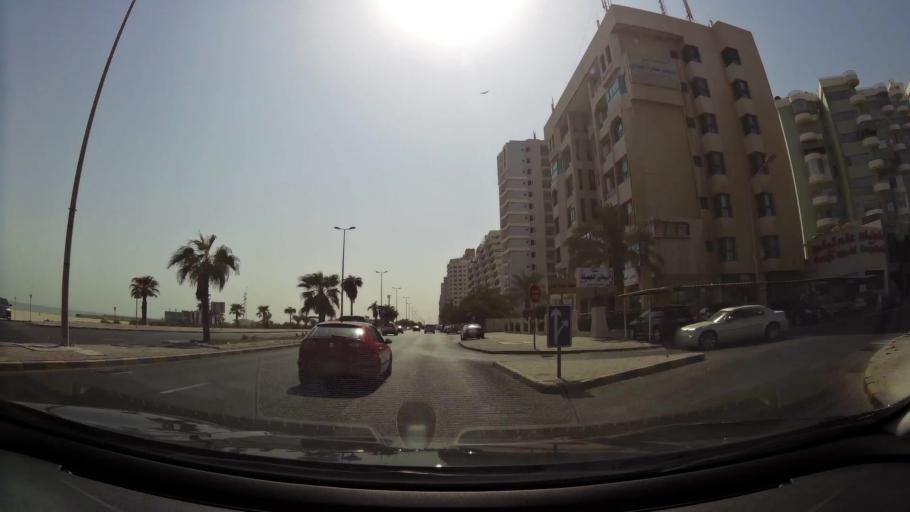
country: KW
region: Muhafazat Hawalli
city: As Salimiyah
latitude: 29.3312
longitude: 48.0920
